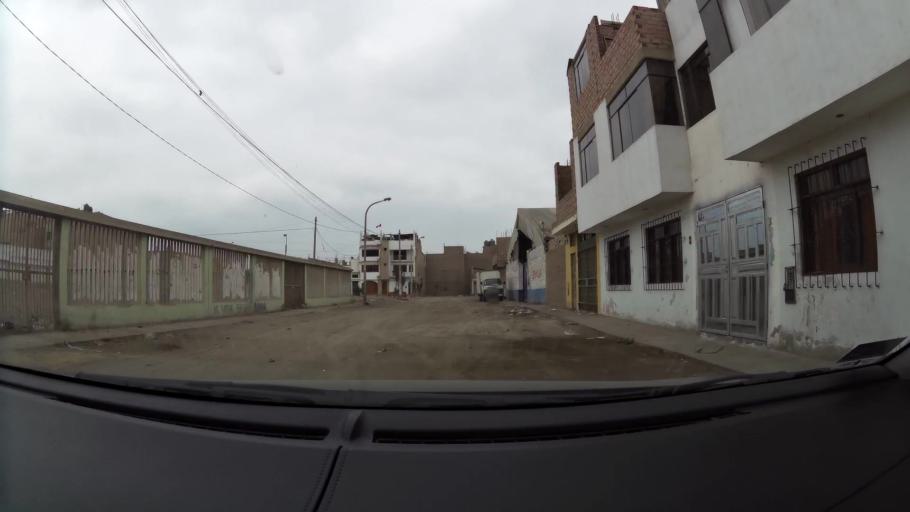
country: PE
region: Lima
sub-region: Provincia de Huaral
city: Huaral
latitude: -11.4957
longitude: -77.1994
